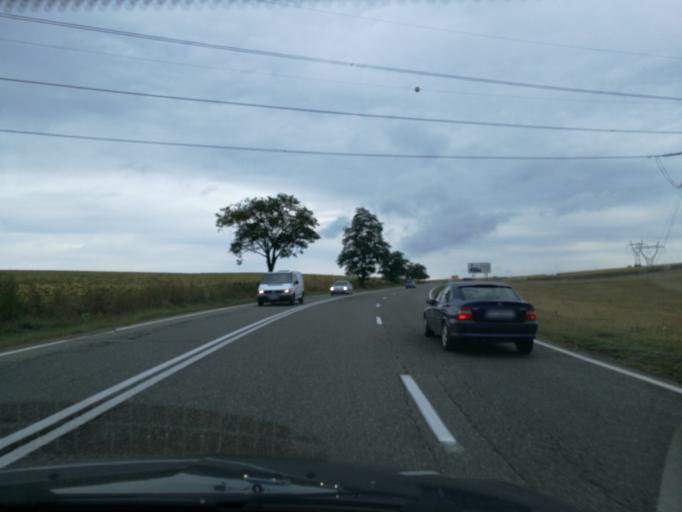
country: RO
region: Suceava
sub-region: Comuna Bunesti
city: Bunesti
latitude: 47.5397
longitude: 26.2700
